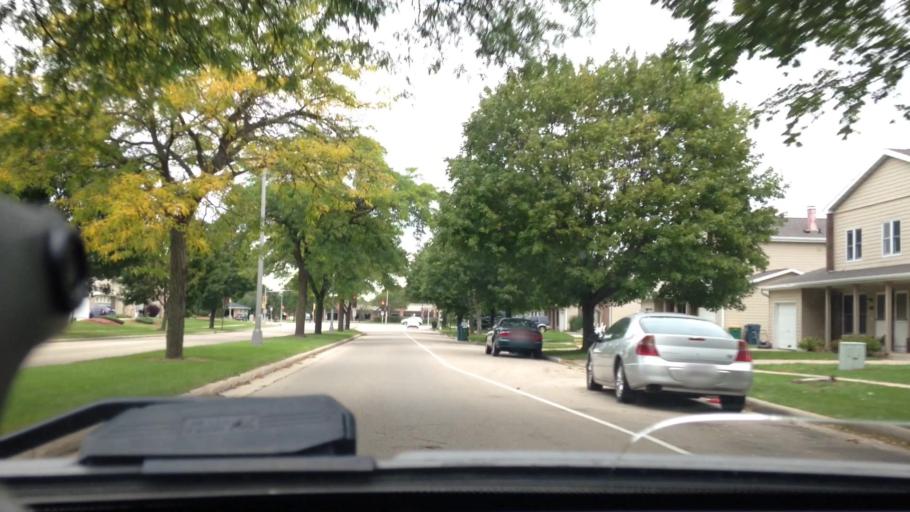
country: US
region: Wisconsin
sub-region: Fond du Lac County
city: North Fond du Lac
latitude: 43.7900
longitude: -88.4729
